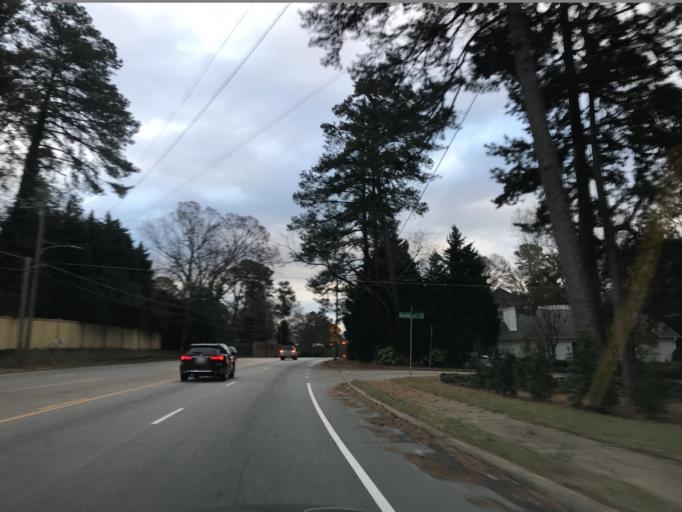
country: US
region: North Carolina
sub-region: Wake County
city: West Raleigh
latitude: 35.8146
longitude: -78.6525
